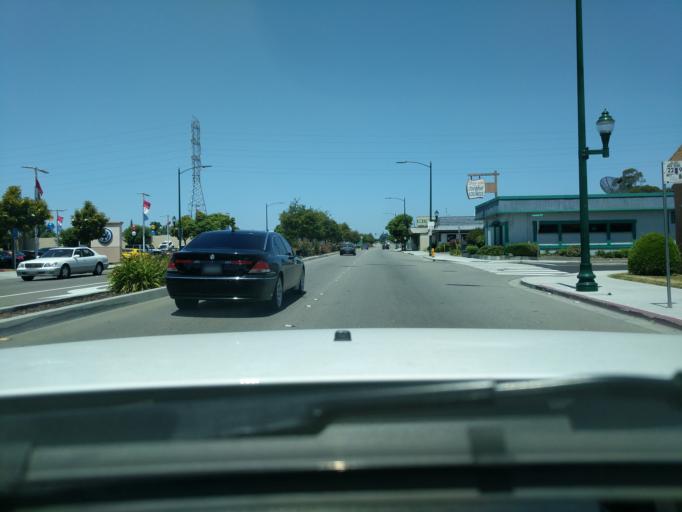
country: US
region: California
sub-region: Alameda County
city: Hayward
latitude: 37.6575
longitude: -122.0718
